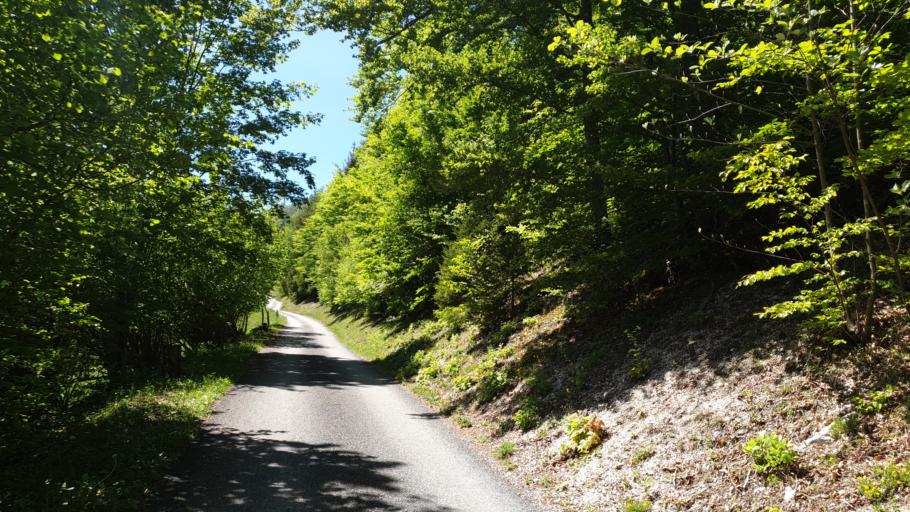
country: CH
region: Solothurn
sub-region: Bezirk Lebern
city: Selzach
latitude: 47.2619
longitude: 7.4587
